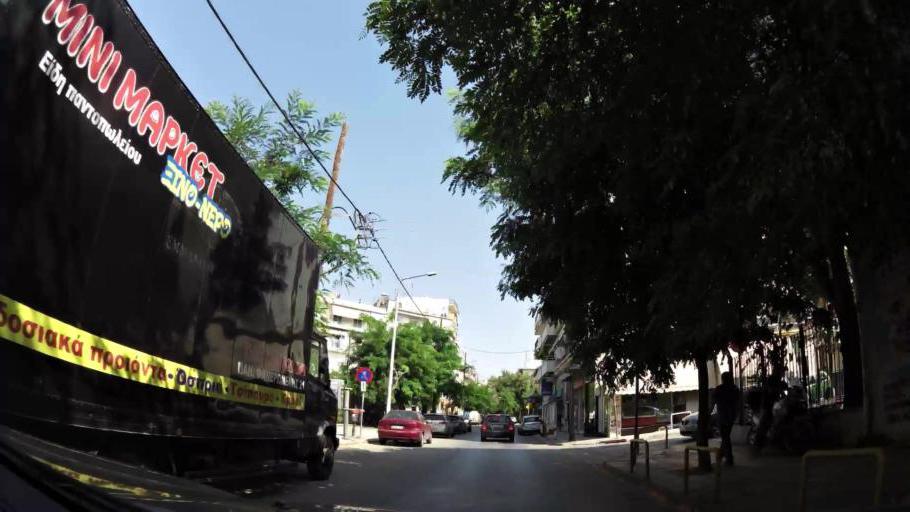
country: GR
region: Central Macedonia
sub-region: Nomos Thessalonikis
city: Thessaloniki
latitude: 40.6459
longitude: 22.9388
